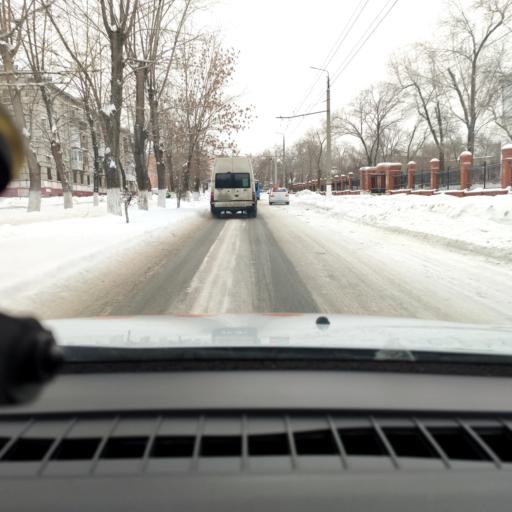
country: RU
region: Samara
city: Novokuybyshevsk
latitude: 53.0962
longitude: 49.9532
